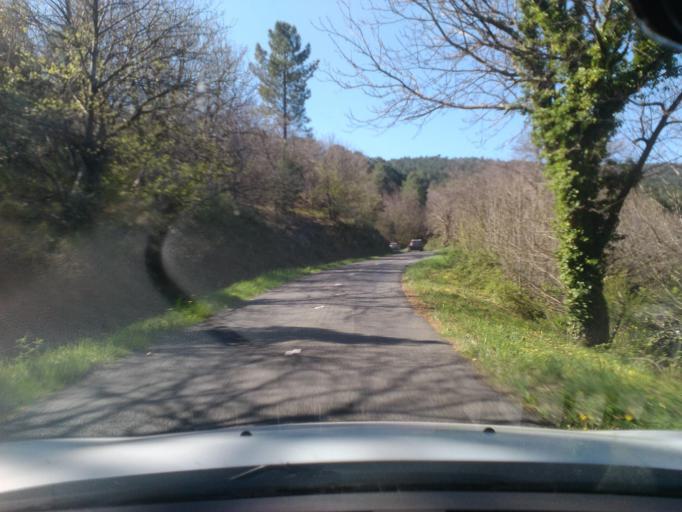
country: FR
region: Languedoc-Roussillon
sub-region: Departement du Gard
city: Valleraugue
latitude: 44.1640
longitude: 3.7505
